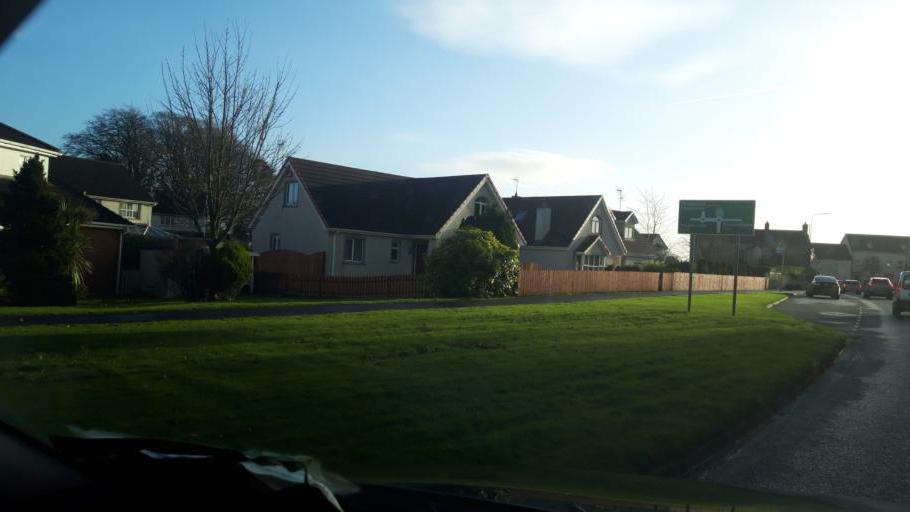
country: GB
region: Northern Ireland
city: Maghera
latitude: 54.8127
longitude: -6.7061
